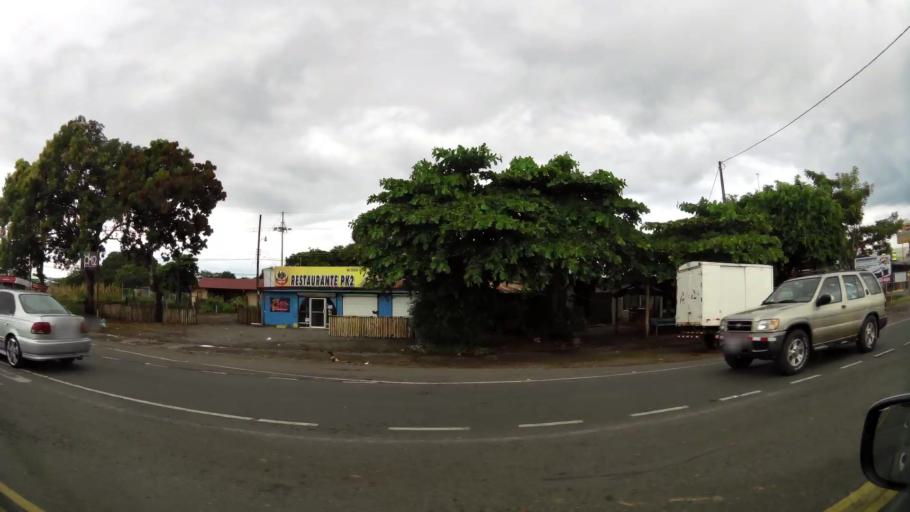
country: CR
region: Puntarenas
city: Esparza
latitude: 9.9959
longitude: -84.6620
